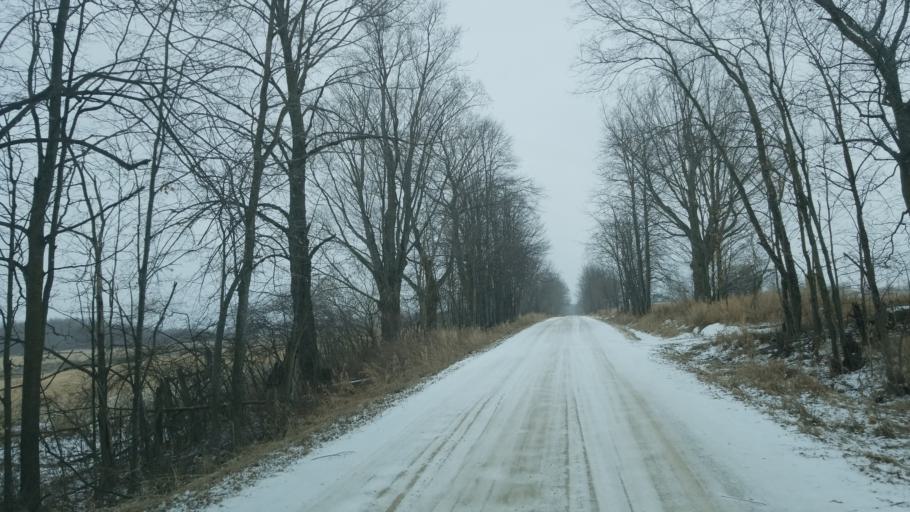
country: US
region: Michigan
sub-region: Osceola County
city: Evart
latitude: 44.0159
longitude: -85.2169
